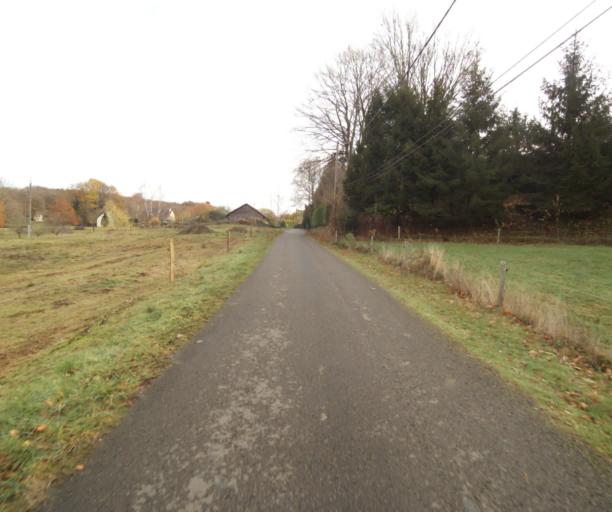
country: FR
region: Limousin
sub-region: Departement de la Correze
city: Cornil
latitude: 45.1763
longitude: 1.7299
